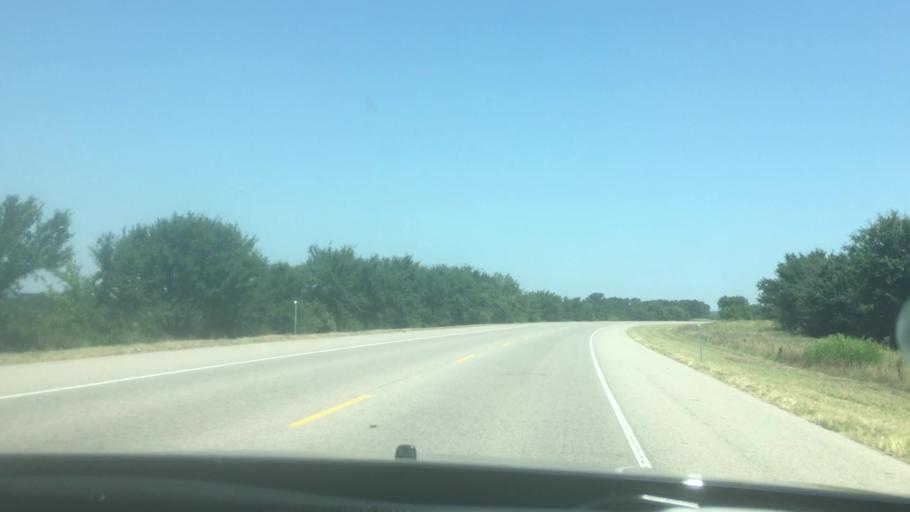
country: US
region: Oklahoma
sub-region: Pontotoc County
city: Ada
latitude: 34.6878
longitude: -96.5940
